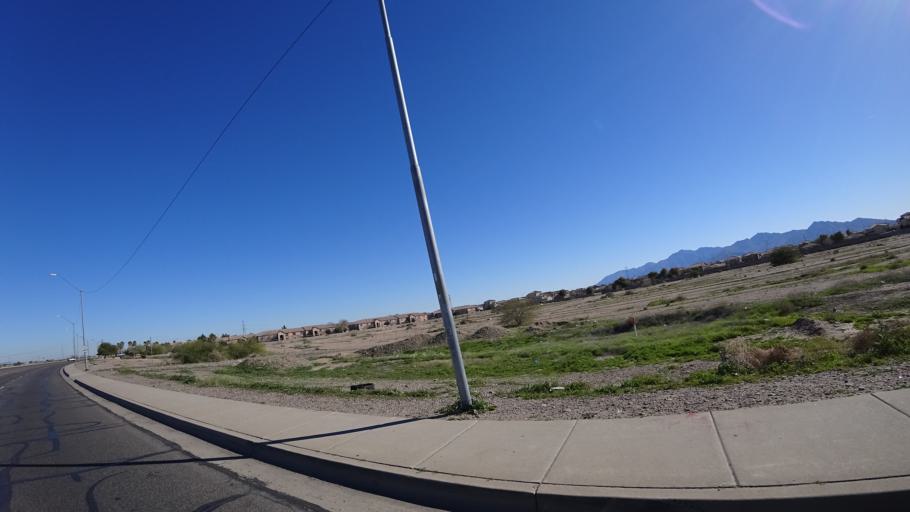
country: US
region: Arizona
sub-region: Maricopa County
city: Avondale
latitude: 33.4343
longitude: -112.3398
